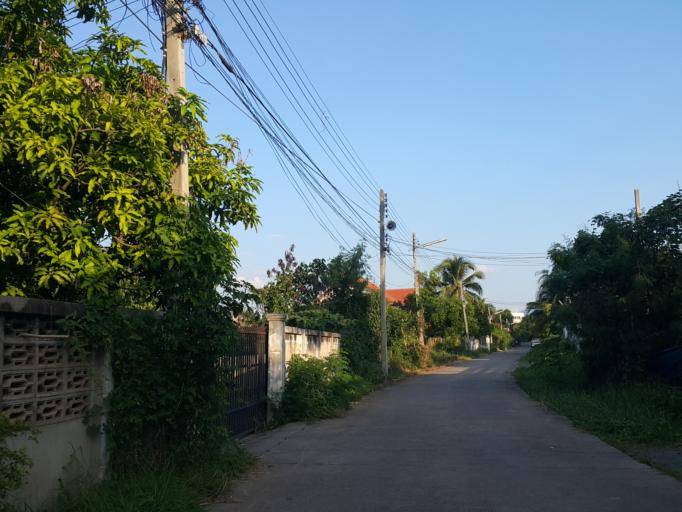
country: TH
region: Chiang Mai
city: San Kamphaeng
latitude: 18.7478
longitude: 99.1168
